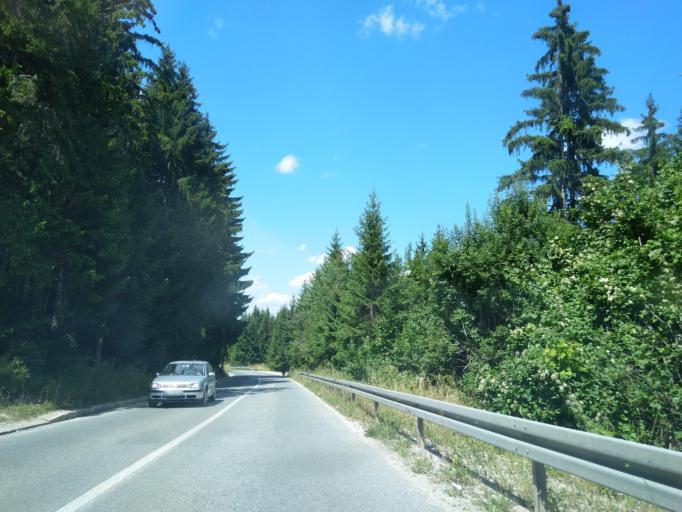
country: RS
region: Central Serbia
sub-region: Zlatiborski Okrug
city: Nova Varos
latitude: 43.4103
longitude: 19.8376
